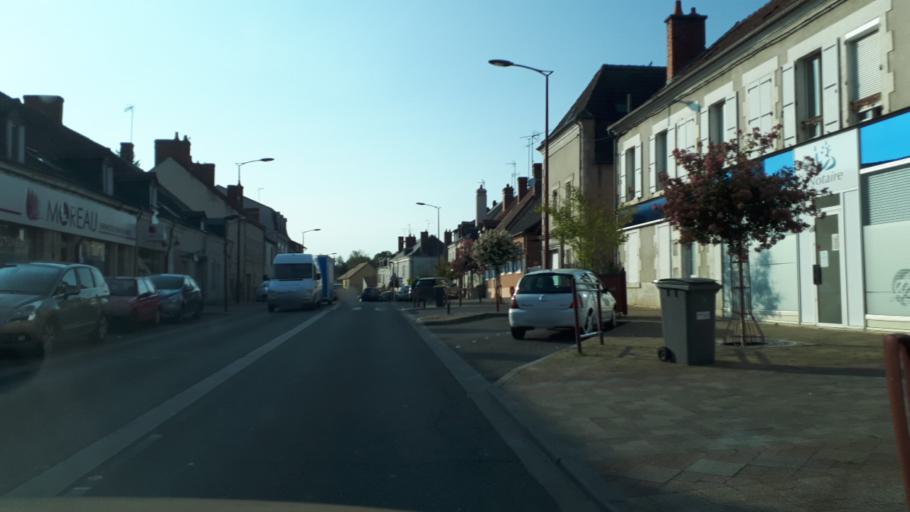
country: FR
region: Centre
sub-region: Departement du Cher
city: Vierzon
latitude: 47.2170
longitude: 2.1013
